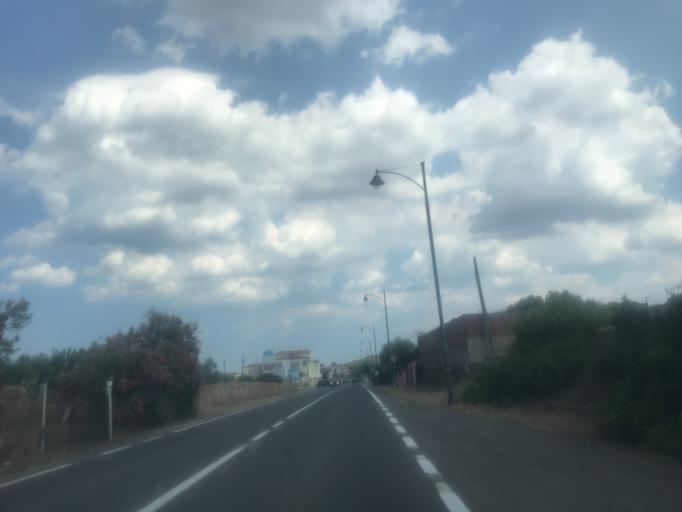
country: IT
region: Sardinia
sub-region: Provincia di Olbia-Tempio
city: Olbia
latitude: 40.8913
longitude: 9.5834
